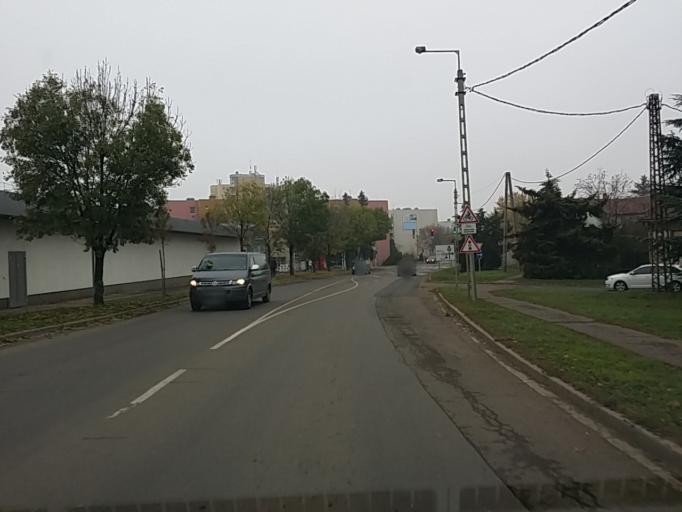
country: HU
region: Heves
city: Gyongyos
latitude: 47.7897
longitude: 19.9371
